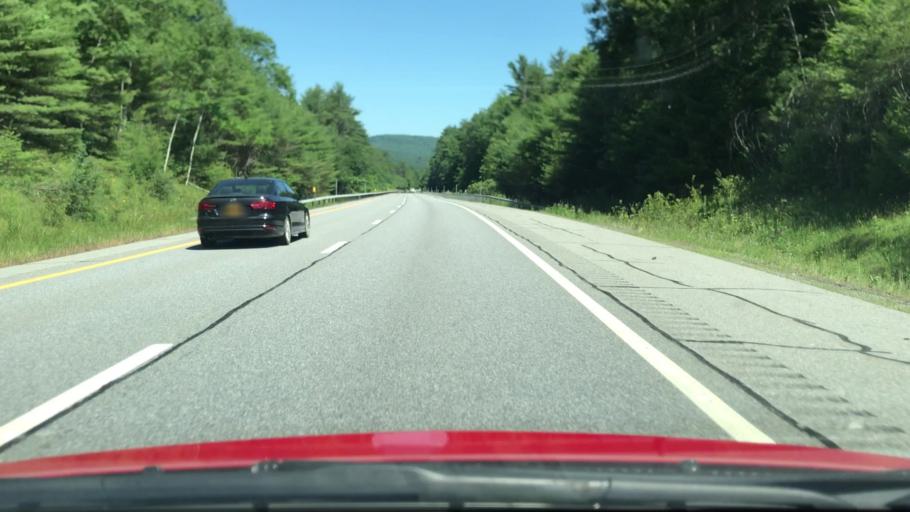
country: US
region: New York
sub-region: Warren County
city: Warrensburg
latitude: 43.5249
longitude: -73.7383
